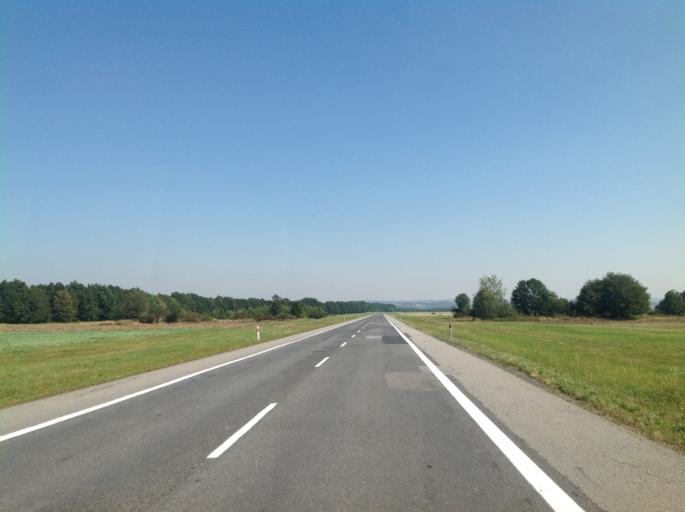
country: PL
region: Opole Voivodeship
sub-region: Powiat nyski
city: Kamienica
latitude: 50.4513
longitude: 16.9205
